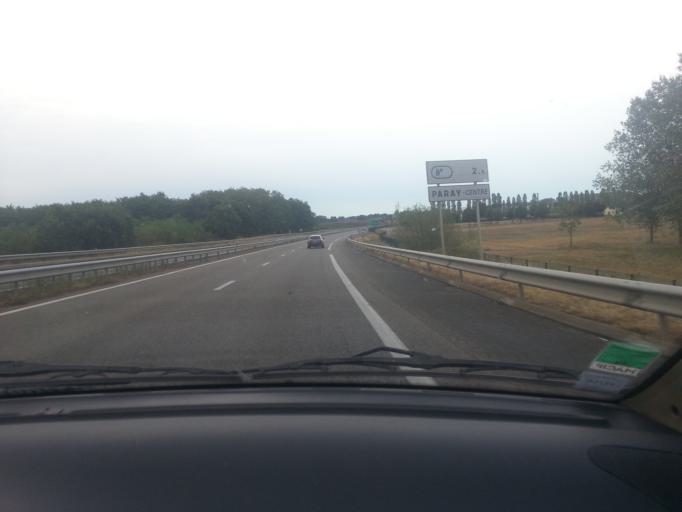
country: FR
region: Bourgogne
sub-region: Departement de Saone-et-Loire
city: Paray-le-Monial
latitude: 46.4673
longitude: 4.0914
